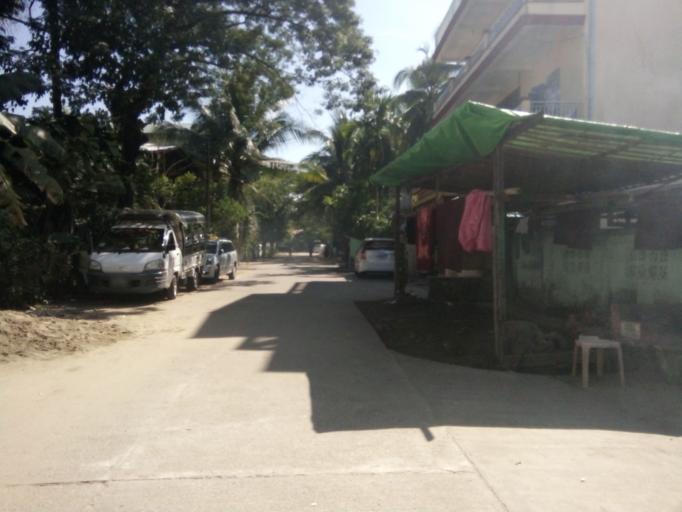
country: MM
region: Yangon
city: Yangon
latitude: 16.9202
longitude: 96.1600
